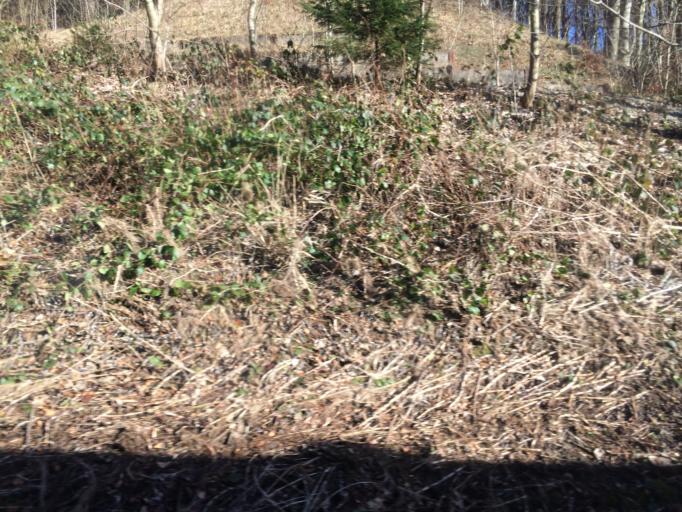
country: DK
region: South Denmark
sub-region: Vejle Kommune
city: Vejle
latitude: 55.7546
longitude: 9.5343
